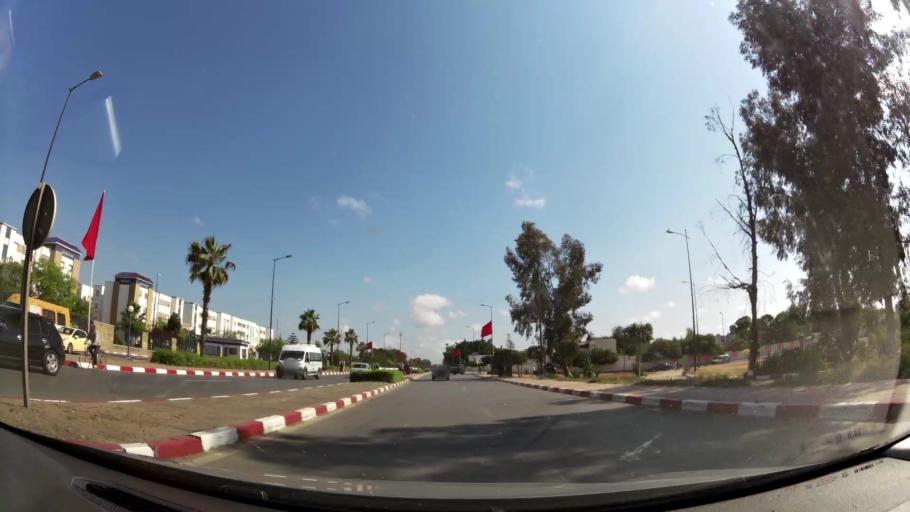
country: MA
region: Rabat-Sale-Zemmour-Zaer
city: Sale
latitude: 34.0425
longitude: -6.7749
